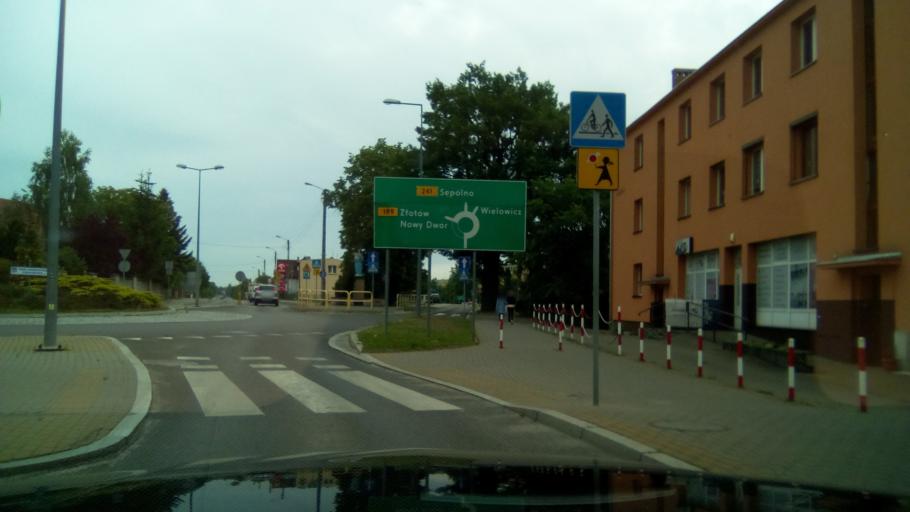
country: PL
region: Kujawsko-Pomorskie
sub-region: Powiat sepolenski
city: Wiecbork
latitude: 53.3569
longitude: 17.4881
